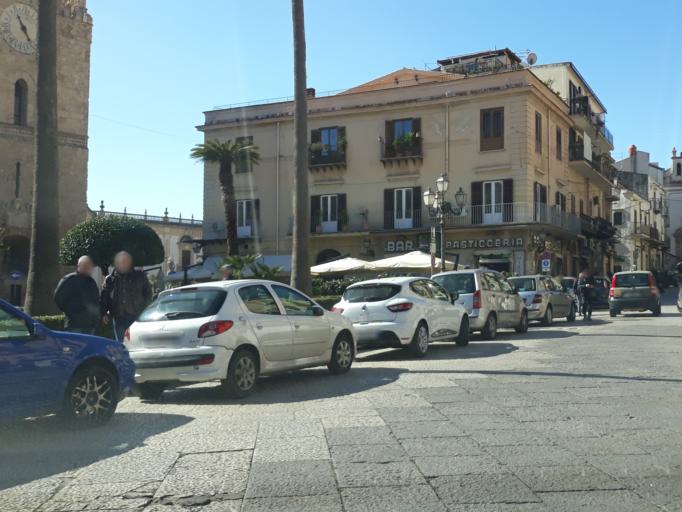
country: IT
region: Sicily
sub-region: Palermo
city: Monreale
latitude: 38.0827
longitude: 13.2919
